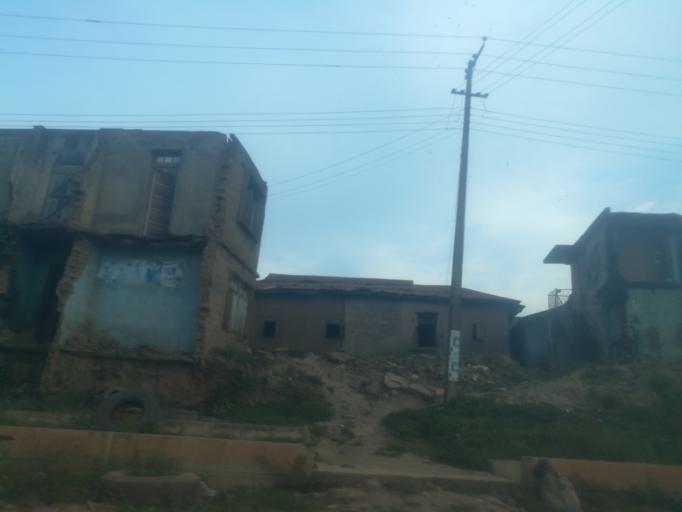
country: NG
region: Ogun
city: Abeokuta
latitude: 7.1710
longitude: 3.3385
